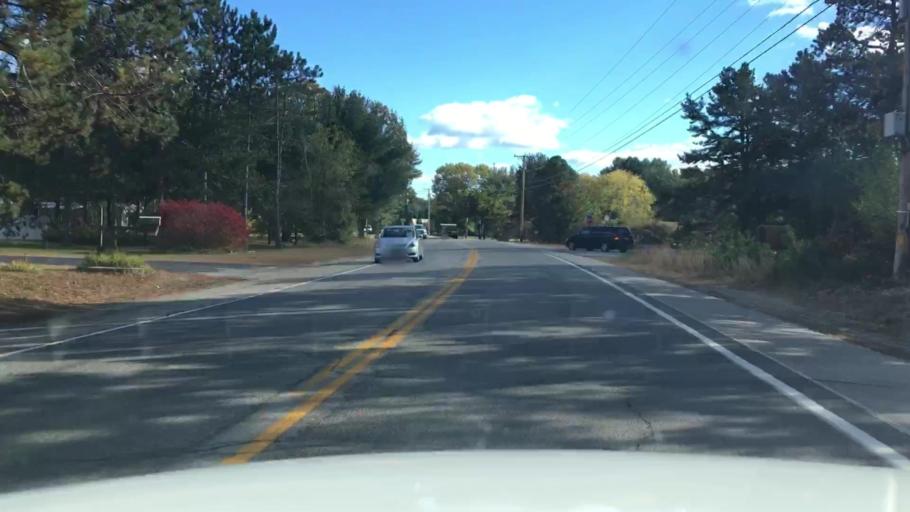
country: US
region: Maine
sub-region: York County
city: South Sanford
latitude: 43.3820
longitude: -70.6879
